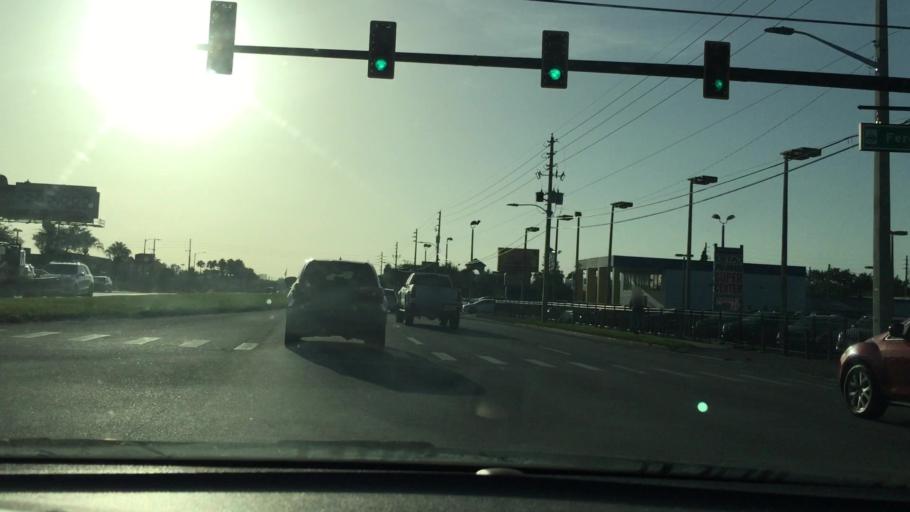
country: US
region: Florida
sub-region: Orange County
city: Pine Hills
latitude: 28.5527
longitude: -81.4200
